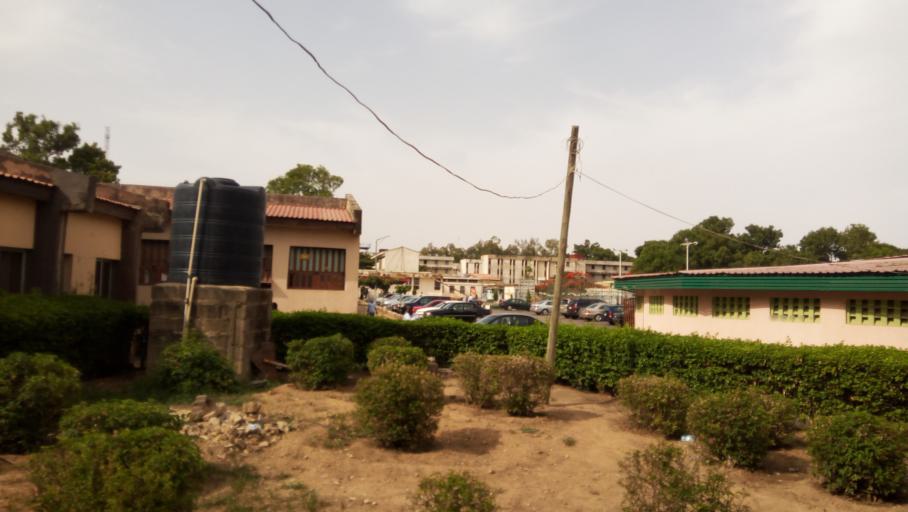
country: NG
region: Kaduna
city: Zaria
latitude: 11.1516
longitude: 7.6547
